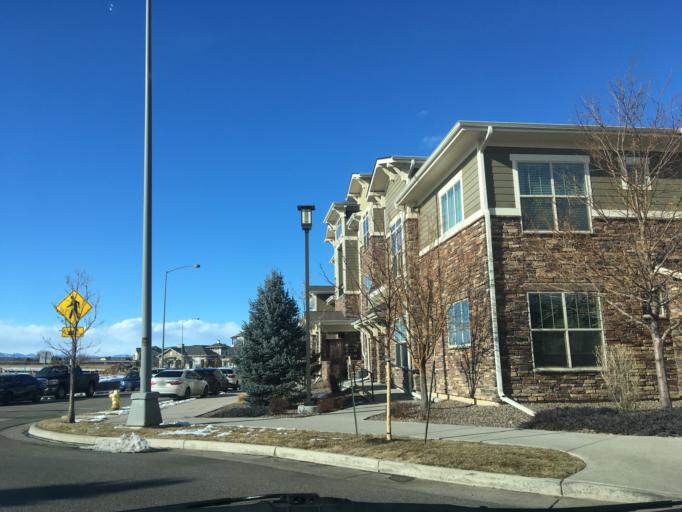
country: US
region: Colorado
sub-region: Boulder County
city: Louisville
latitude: 39.9466
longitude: -105.1219
